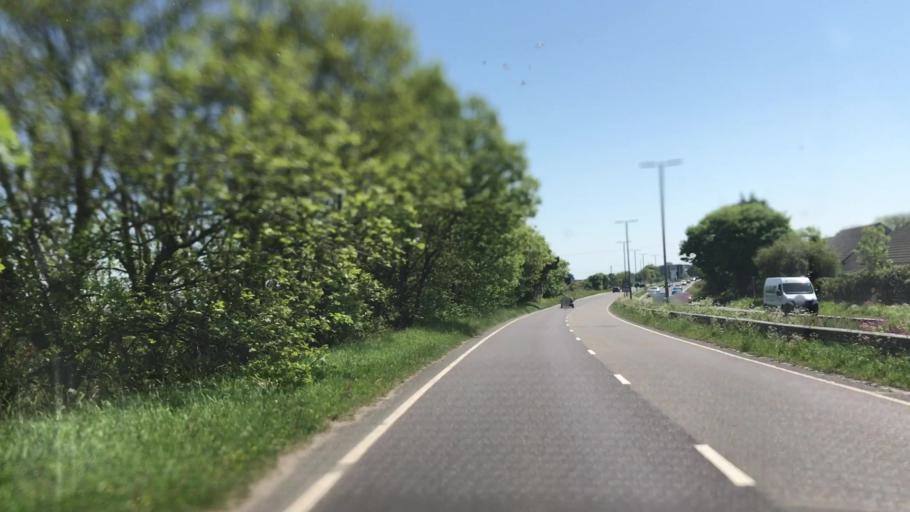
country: GB
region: England
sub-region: Cornwall
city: Chacewater
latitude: 50.2645
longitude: -5.1140
